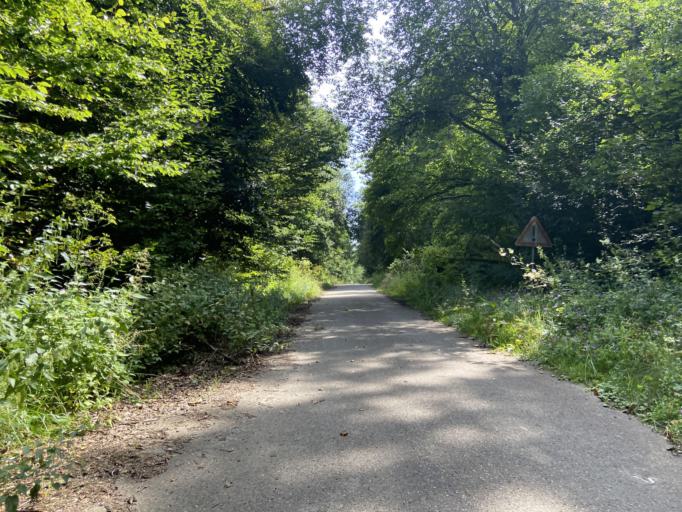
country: DE
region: Baden-Wuerttemberg
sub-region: Tuebingen Region
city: Sigmaringen
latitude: 48.0976
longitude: 9.2441
